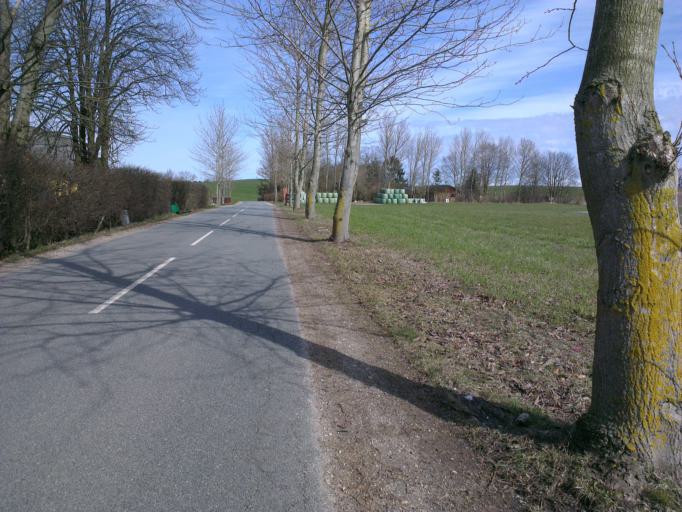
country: DK
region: Capital Region
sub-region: Egedal Kommune
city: Olstykke
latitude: 55.8415
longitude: 12.1245
